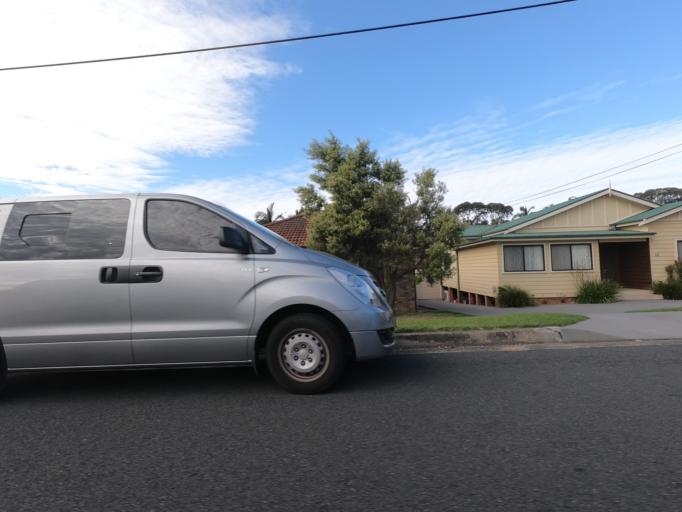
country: AU
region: New South Wales
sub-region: Wollongong
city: Corrimal
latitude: -34.3582
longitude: 150.8979
